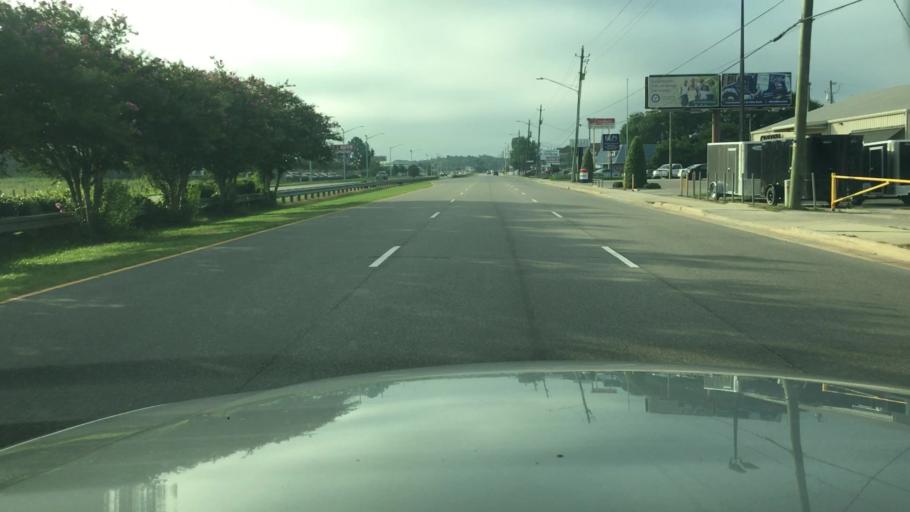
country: US
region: North Carolina
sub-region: Cumberland County
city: Fayetteville
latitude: 35.0822
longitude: -78.9451
